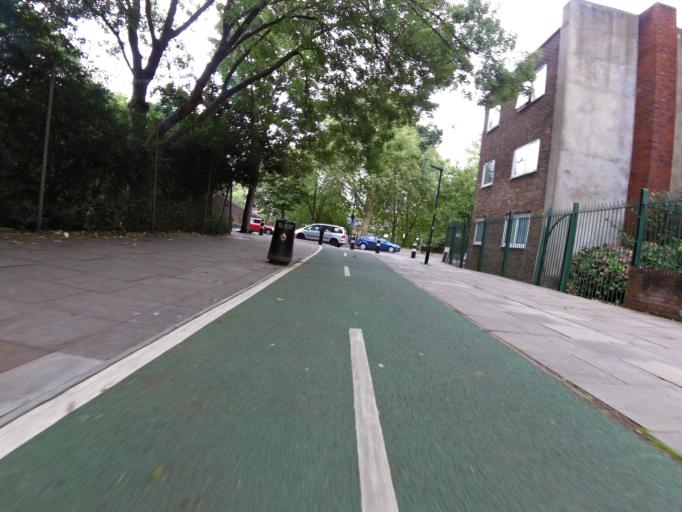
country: GB
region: England
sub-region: Greater London
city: Camden Town
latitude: 51.5325
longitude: -0.1306
